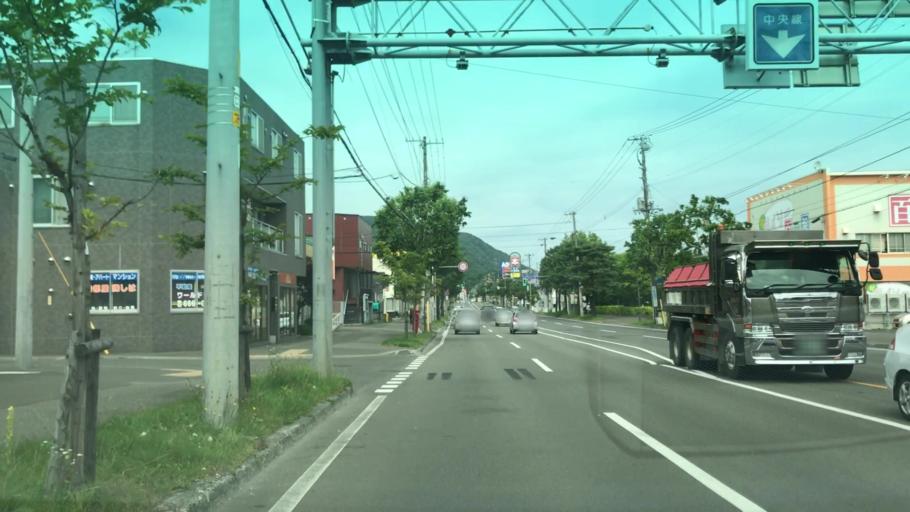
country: JP
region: Hokkaido
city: Sapporo
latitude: 43.0730
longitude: 141.2804
